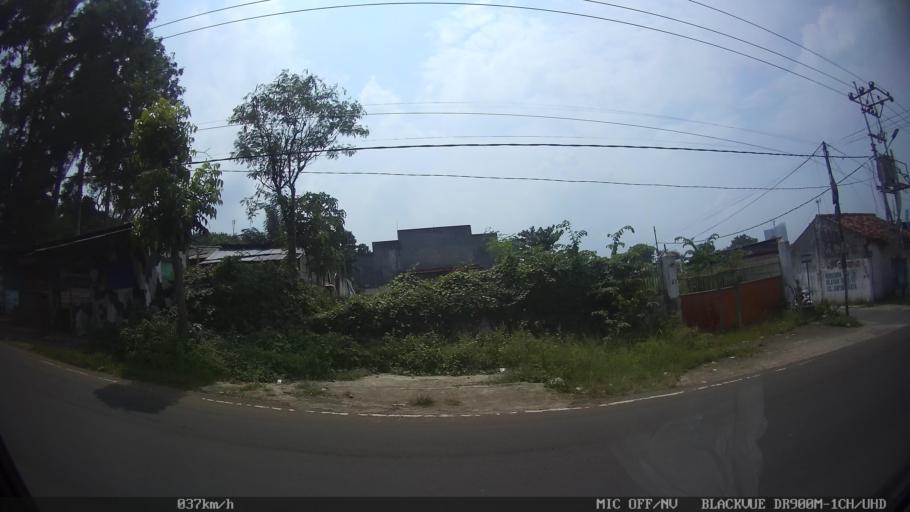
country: ID
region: Lampung
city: Bandarlampung
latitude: -5.4366
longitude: 105.2742
